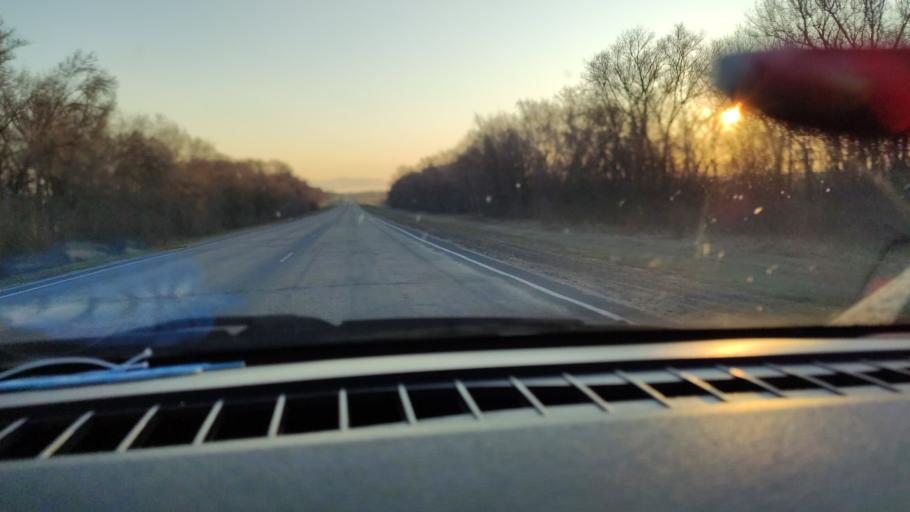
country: RU
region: Saratov
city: Sinodskoye
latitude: 51.9658
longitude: 46.6329
